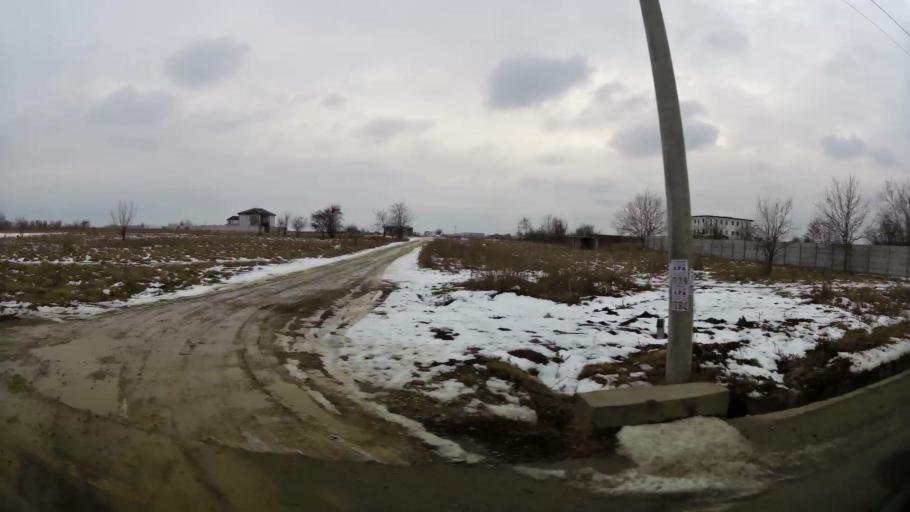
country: RO
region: Ilfov
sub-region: Comuna Tunari
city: Tunari
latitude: 44.5456
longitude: 26.1531
